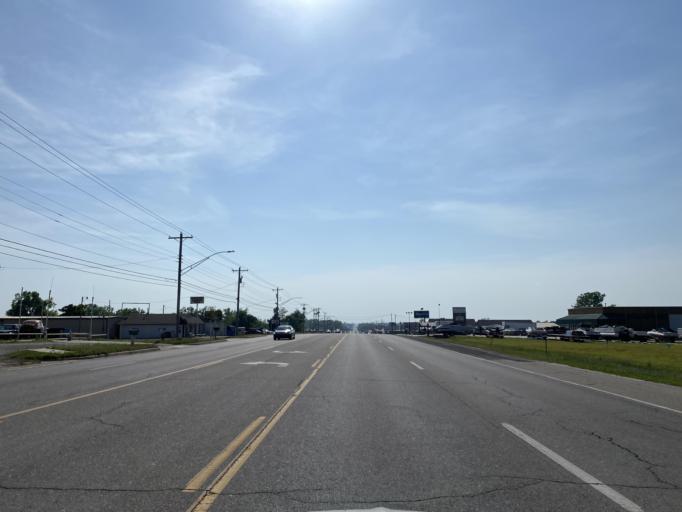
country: US
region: Oklahoma
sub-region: Oklahoma County
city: Nicoma Park
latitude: 35.4931
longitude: -97.3465
